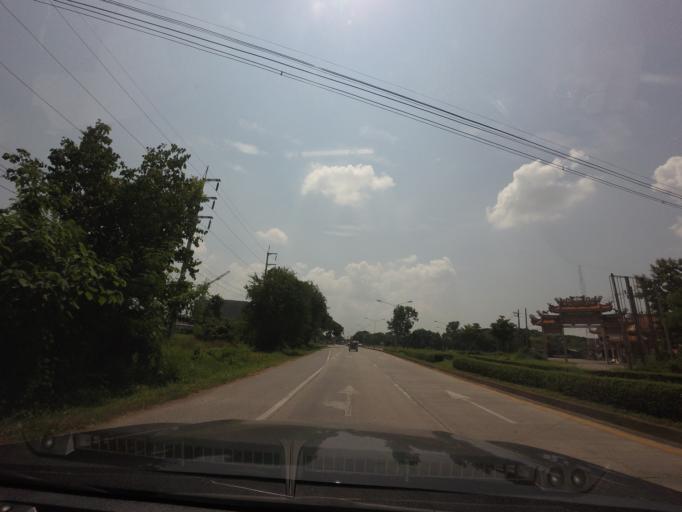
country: TH
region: Uttaradit
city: Uttaradit
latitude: 17.6099
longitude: 100.1233
